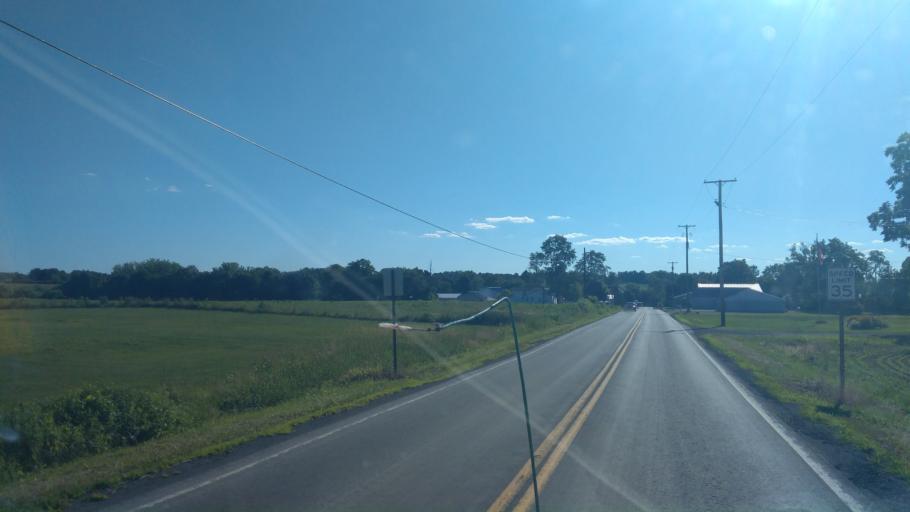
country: US
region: New York
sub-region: Wayne County
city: Lyons
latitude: 42.9958
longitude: -76.9180
